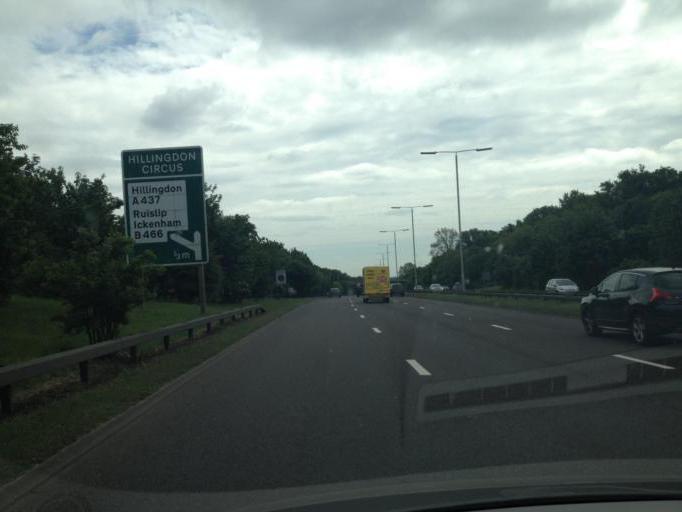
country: GB
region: England
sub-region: Greater London
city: Uxbridge
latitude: 51.5584
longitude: -0.4679
